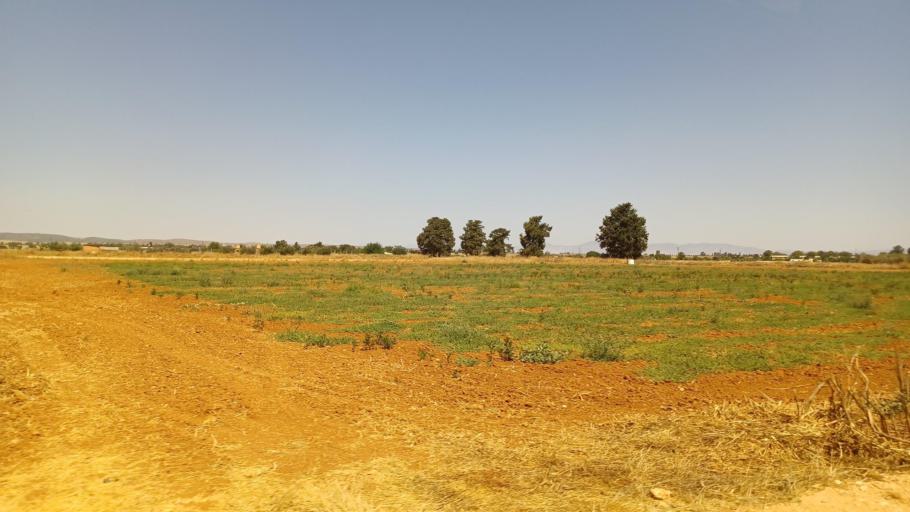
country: CY
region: Larnaka
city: Xylotymbou
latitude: 35.0262
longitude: 33.7362
